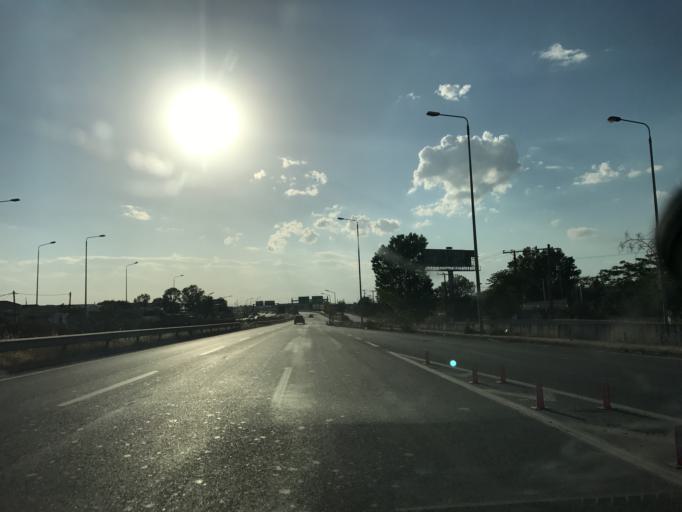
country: GR
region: Central Macedonia
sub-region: Nomos Thessalonikis
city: Menemeni
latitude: 40.6544
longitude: 22.8962
